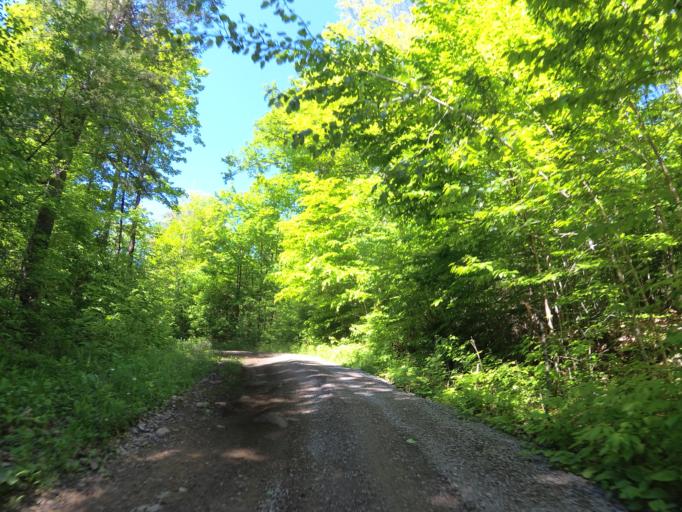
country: CA
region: Ontario
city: Renfrew
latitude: 45.0961
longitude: -77.0667
